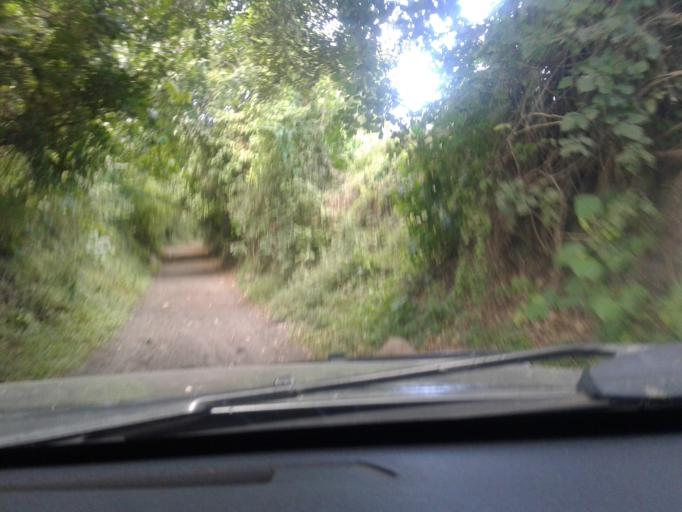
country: NI
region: Rivas
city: Moyogalpa
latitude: 11.5525
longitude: -85.6623
